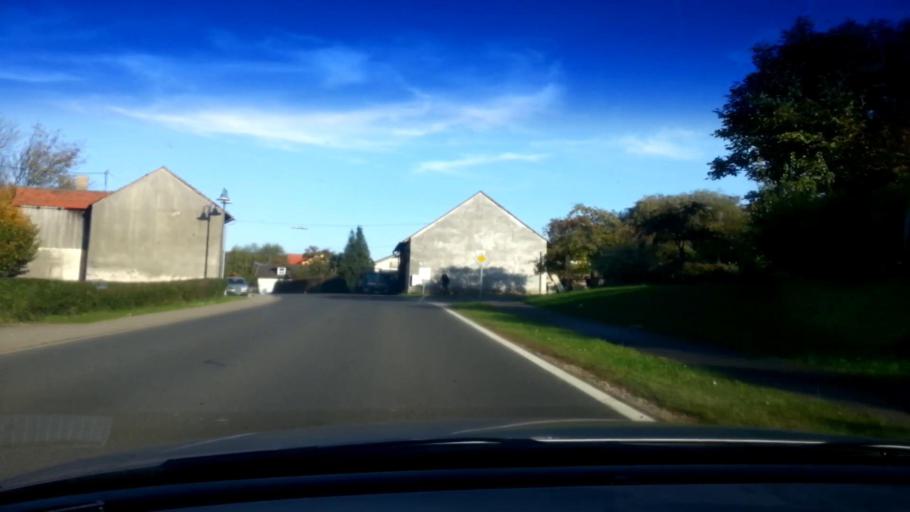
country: DE
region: Bavaria
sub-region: Upper Franconia
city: Litzendorf
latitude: 49.9154
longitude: 11.0416
